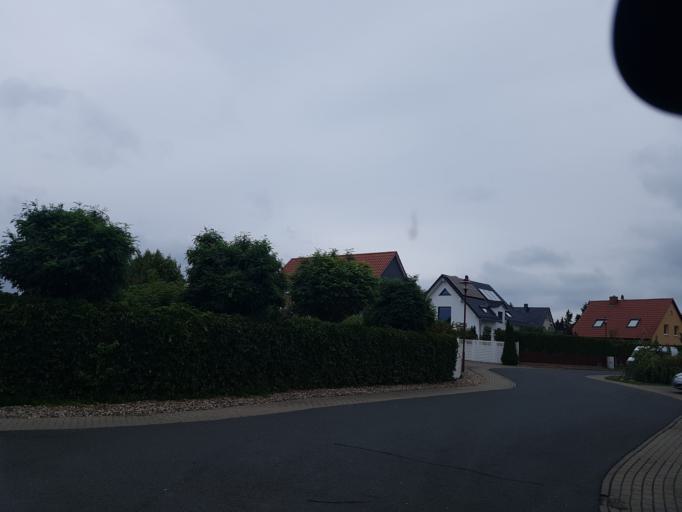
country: DE
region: Saxony-Anhalt
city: Jessen
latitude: 51.7913
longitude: 12.9697
